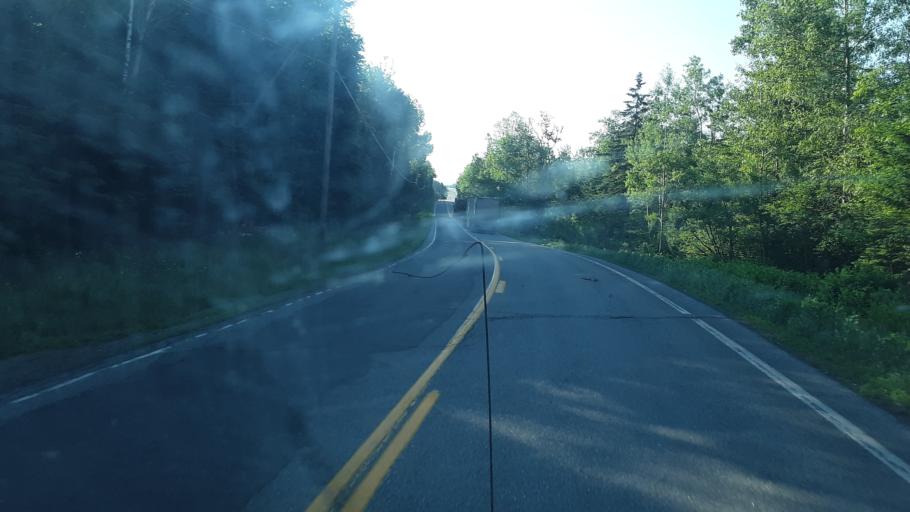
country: US
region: Maine
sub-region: Penobscot County
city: Patten
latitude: 46.1437
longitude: -68.2083
